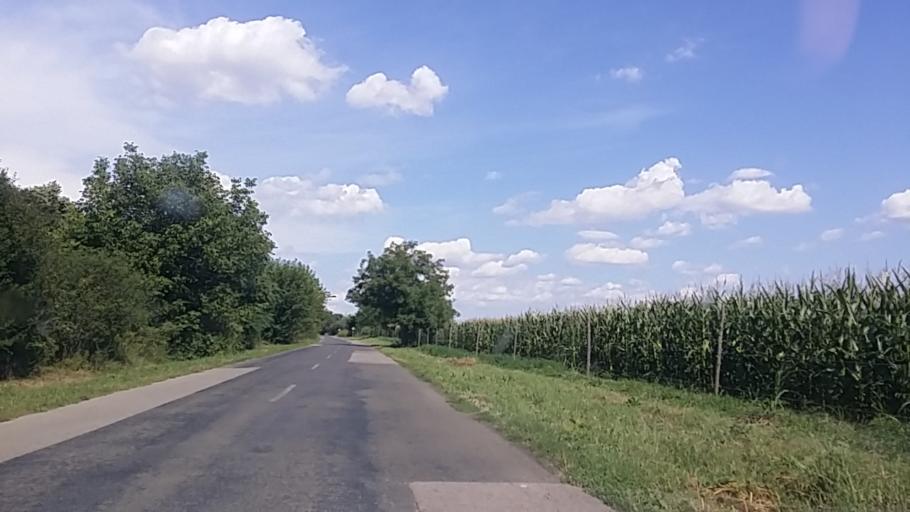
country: HU
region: Tolna
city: Gyonk
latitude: 46.5370
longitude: 18.4524
